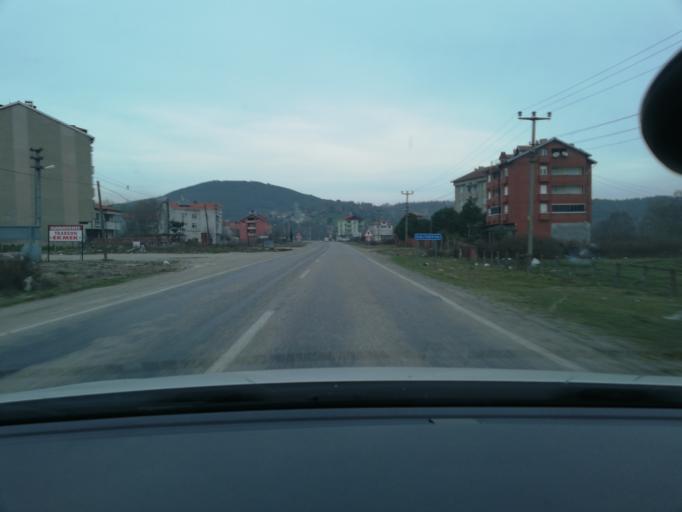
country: TR
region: Zonguldak
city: Saltukova
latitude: 41.5229
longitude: 32.1015
